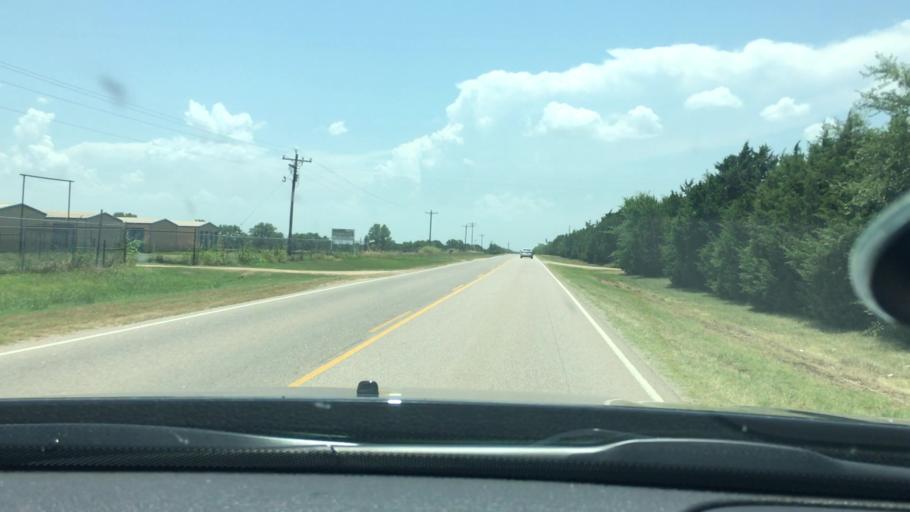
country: US
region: Oklahoma
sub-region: Johnston County
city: Tishomingo
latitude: 34.2823
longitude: -96.6711
